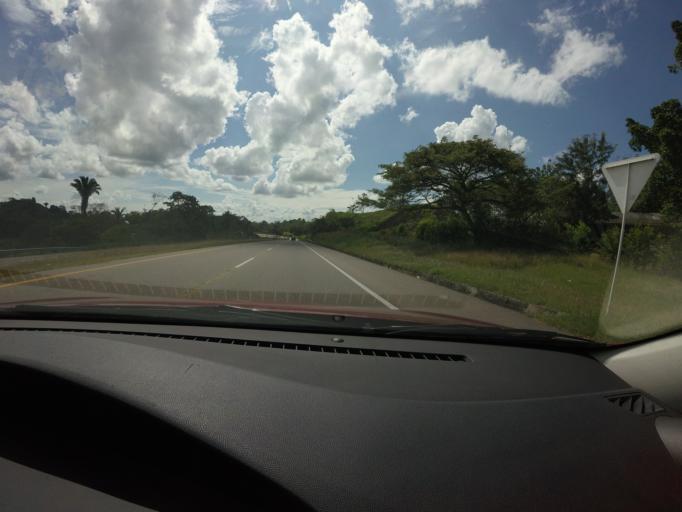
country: CO
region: Antioquia
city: Puerto Triunfo
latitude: 5.8331
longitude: -74.5823
